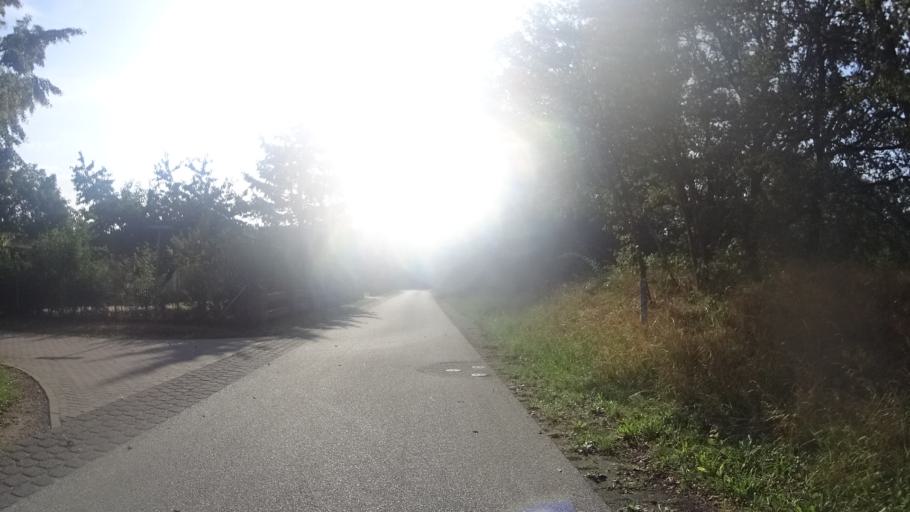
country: DE
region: Brandenburg
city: Cumlosen
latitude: 53.0257
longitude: 11.6786
